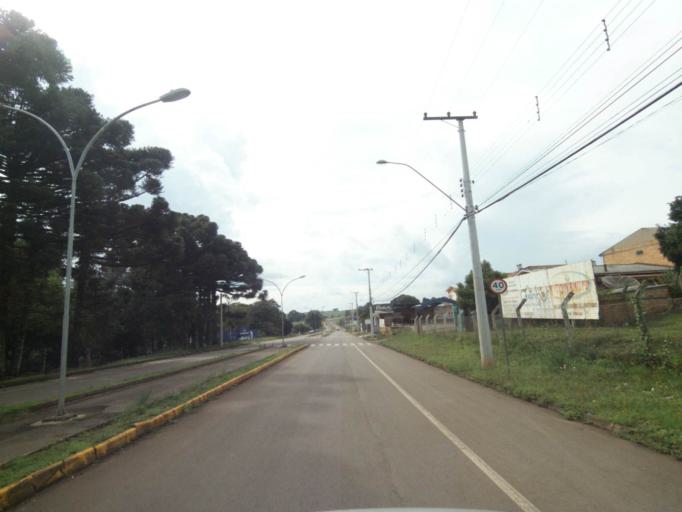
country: BR
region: Rio Grande do Sul
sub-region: Lagoa Vermelha
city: Lagoa Vermelha
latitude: -28.2222
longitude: -51.5119
